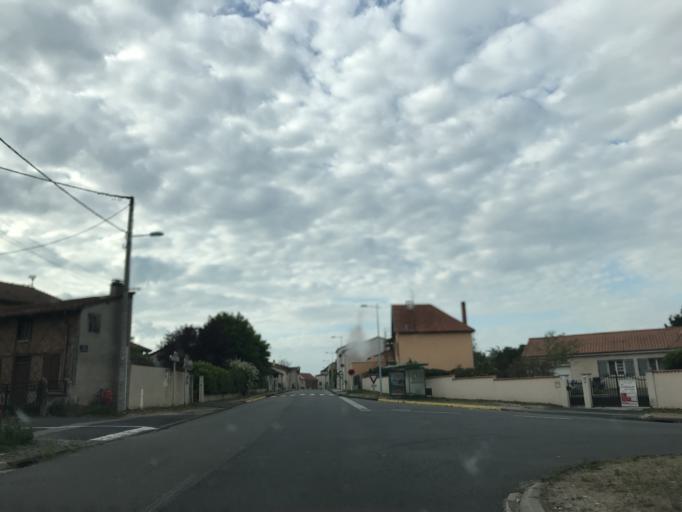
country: FR
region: Auvergne
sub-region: Departement du Puy-de-Dome
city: Randan
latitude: 46.0094
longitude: 3.3522
